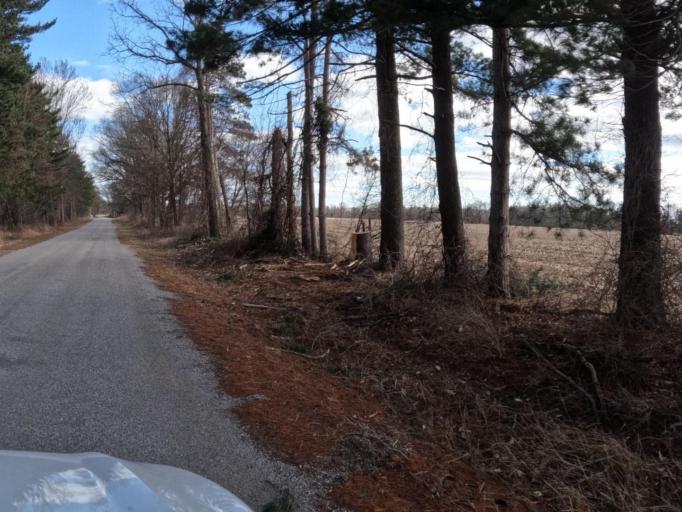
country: CA
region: Ontario
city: Norfolk County
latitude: 42.7498
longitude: -80.2992
